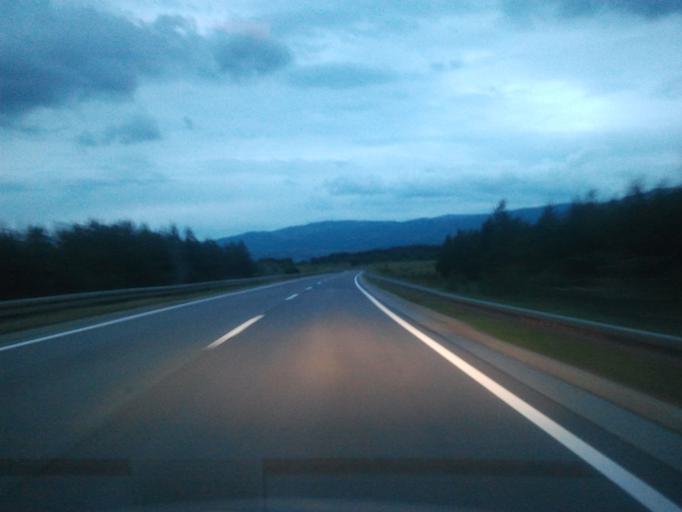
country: HR
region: Zadarska
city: Gracac
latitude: 44.5229
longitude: 15.7463
